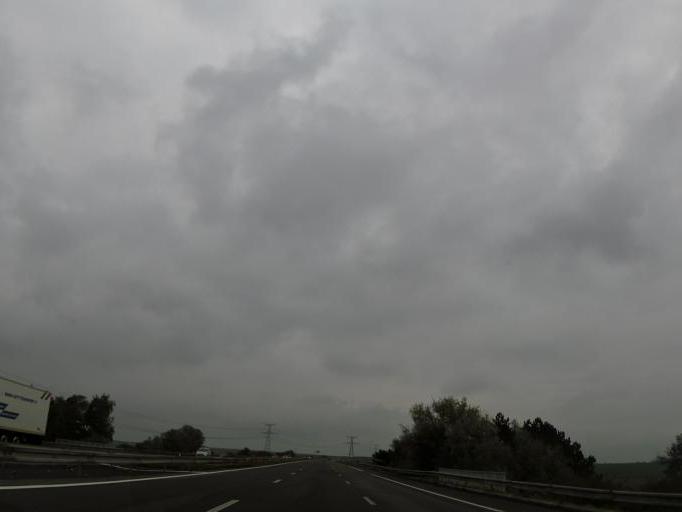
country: FR
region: Lorraine
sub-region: Departement de la Moselle
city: Boulay-Moselle
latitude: 49.1407
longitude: 6.4675
